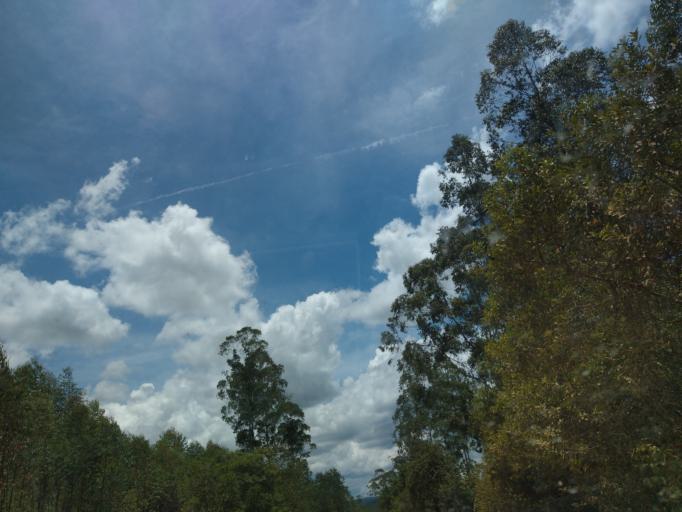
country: BR
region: Minas Gerais
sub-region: Sao Joao Del Rei
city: Sao Joao del Rei
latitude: -20.9053
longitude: -44.2901
